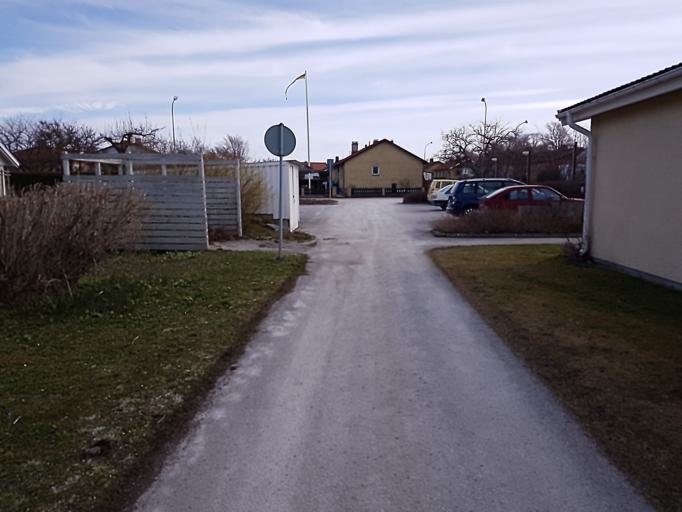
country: SE
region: Gotland
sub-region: Gotland
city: Visby
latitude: 57.6351
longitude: 18.3147
